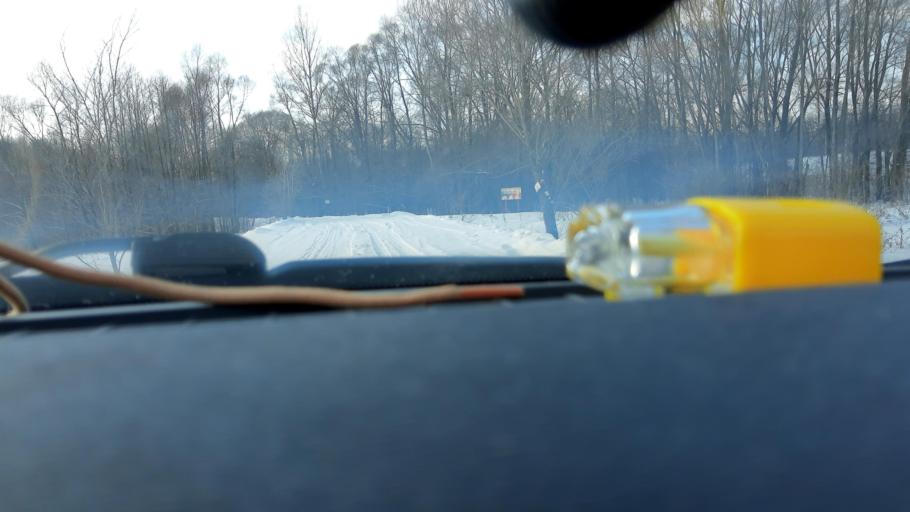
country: RU
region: Bashkortostan
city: Kabakovo
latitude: 54.6350
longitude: 56.0612
